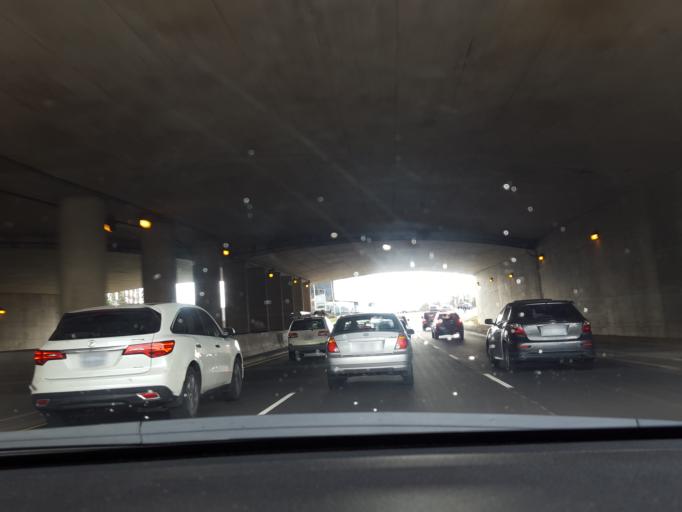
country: CA
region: Ontario
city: Brampton
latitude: 43.6032
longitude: -79.7553
